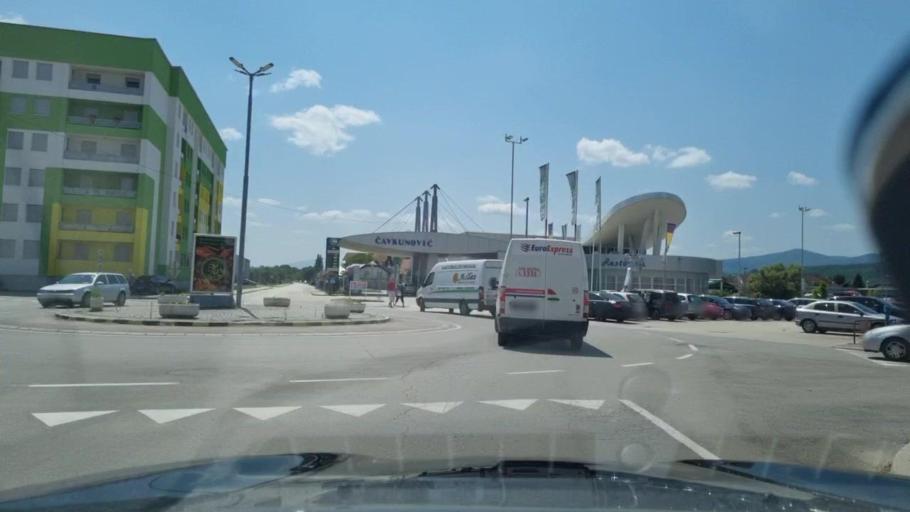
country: BA
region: Federation of Bosnia and Herzegovina
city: Sanski Most
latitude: 44.7632
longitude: 16.6730
